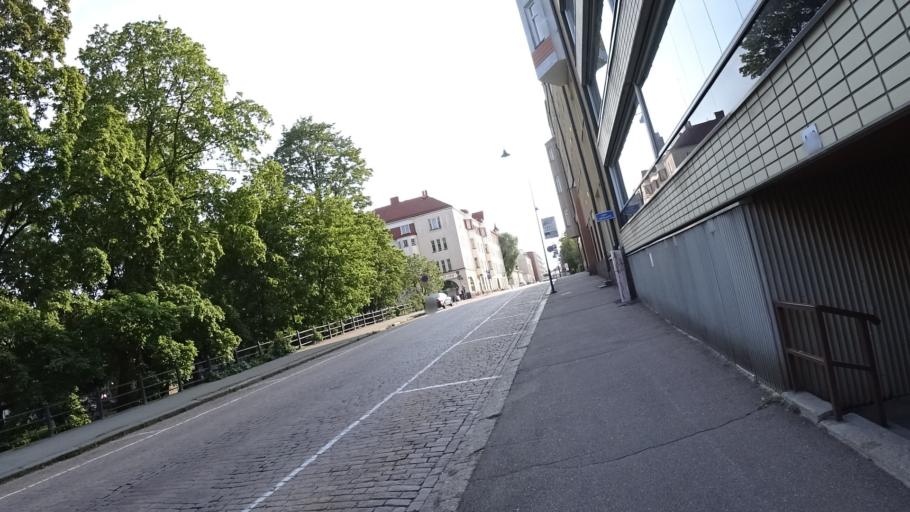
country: FI
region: Kymenlaakso
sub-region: Kotka-Hamina
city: Kotka
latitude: 60.4661
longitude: 26.9410
